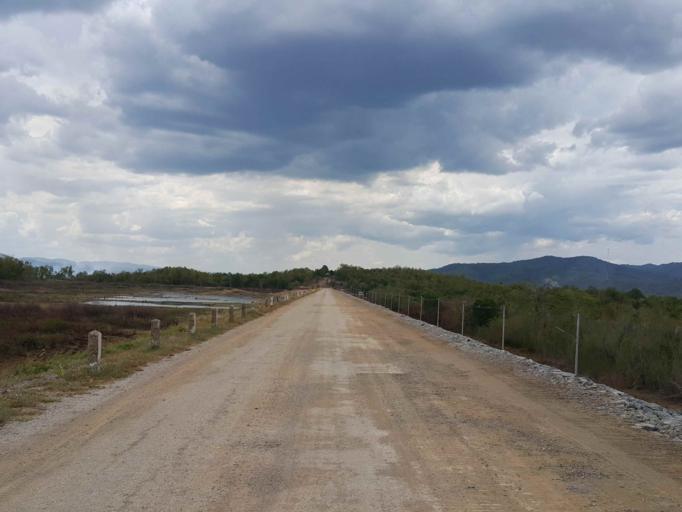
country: TH
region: Sukhothai
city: Thung Saliam
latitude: 17.3195
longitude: 99.4236
